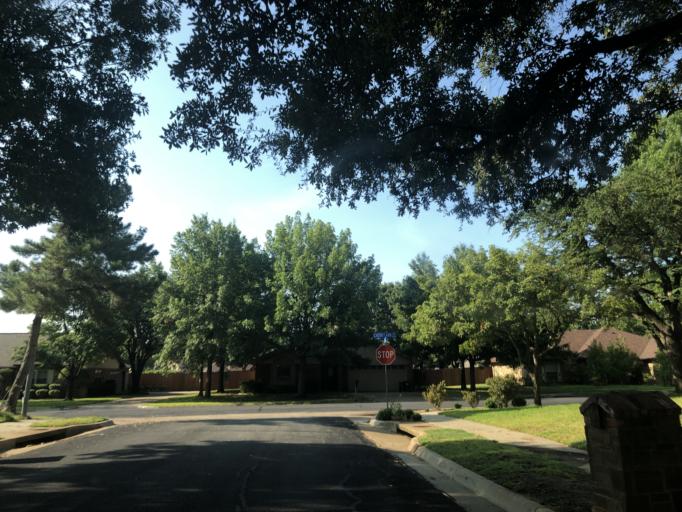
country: US
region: Texas
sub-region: Tarrant County
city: Euless
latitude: 32.8727
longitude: -97.0894
